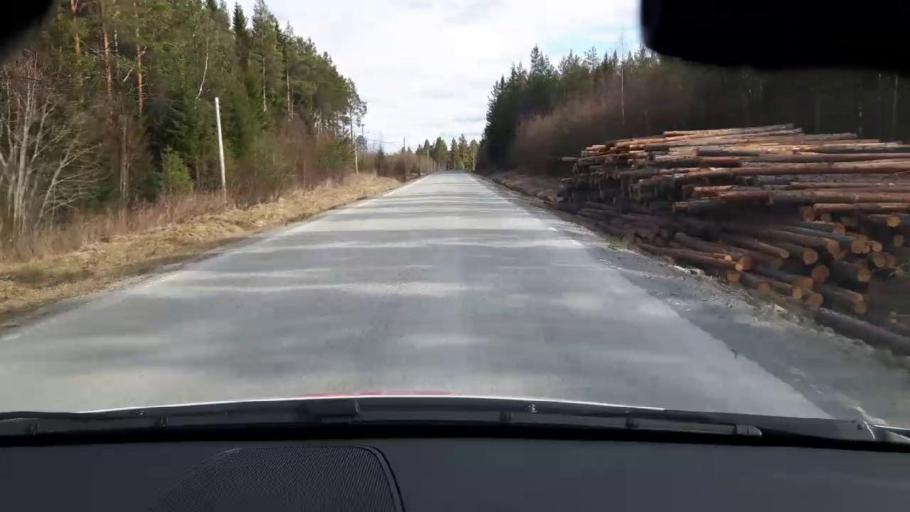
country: SE
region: Jaemtland
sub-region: Bergs Kommun
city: Hoverberg
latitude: 62.7364
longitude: 14.5910
